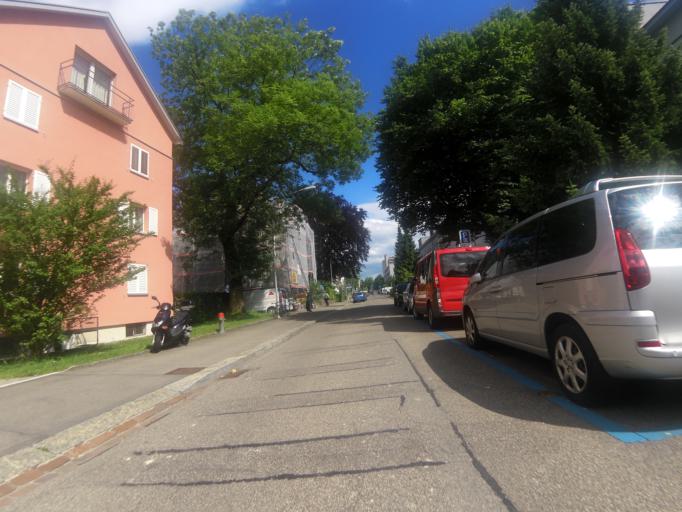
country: CH
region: Zurich
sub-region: Bezirk Zuerich
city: Zuerich (Kreis 9) / Albisrieden
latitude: 47.3765
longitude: 8.4938
